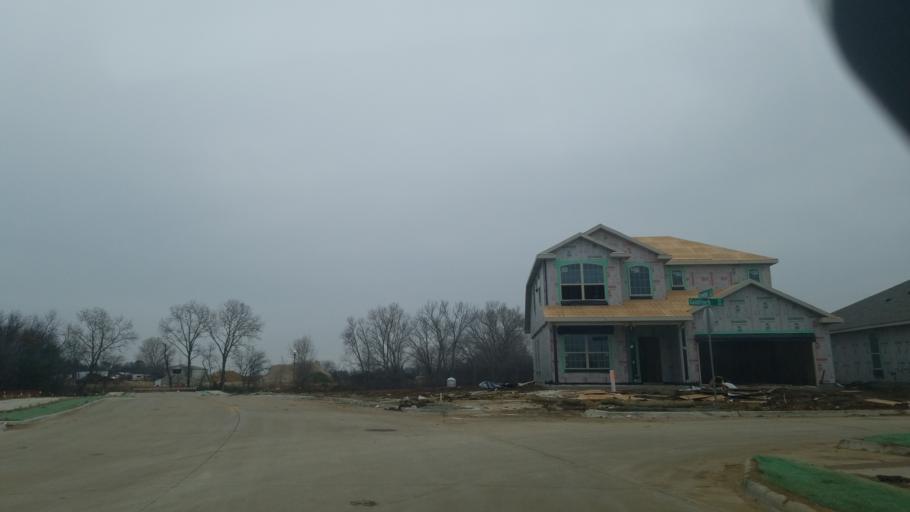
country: US
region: Texas
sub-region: Denton County
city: Denton
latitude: 33.1567
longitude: -97.1354
